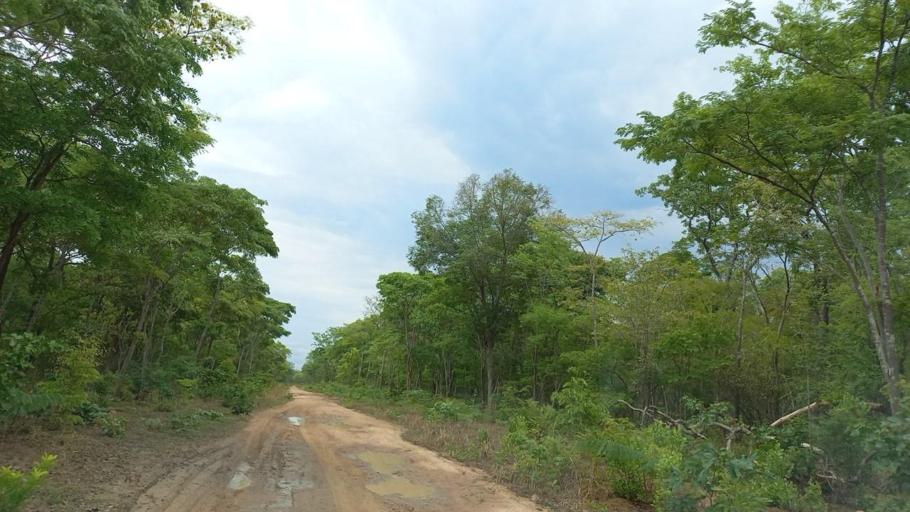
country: ZM
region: North-Western
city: Kalengwa
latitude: -13.5570
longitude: 24.9739
